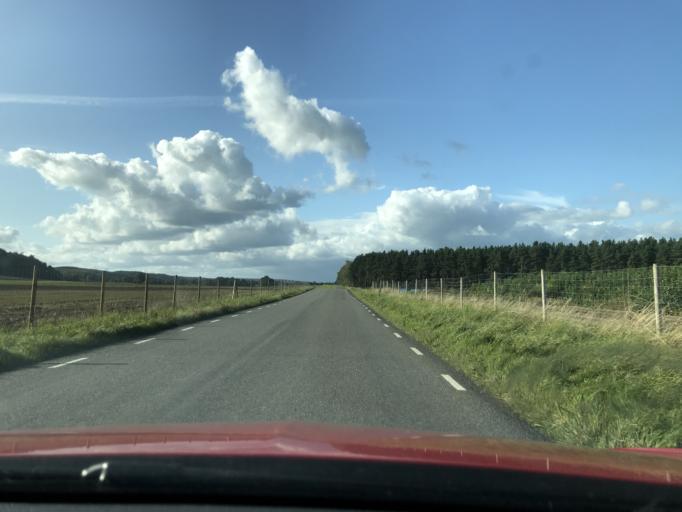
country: SE
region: Skane
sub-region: Kristianstads Kommun
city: Degeberga
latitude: 55.8549
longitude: 14.0731
